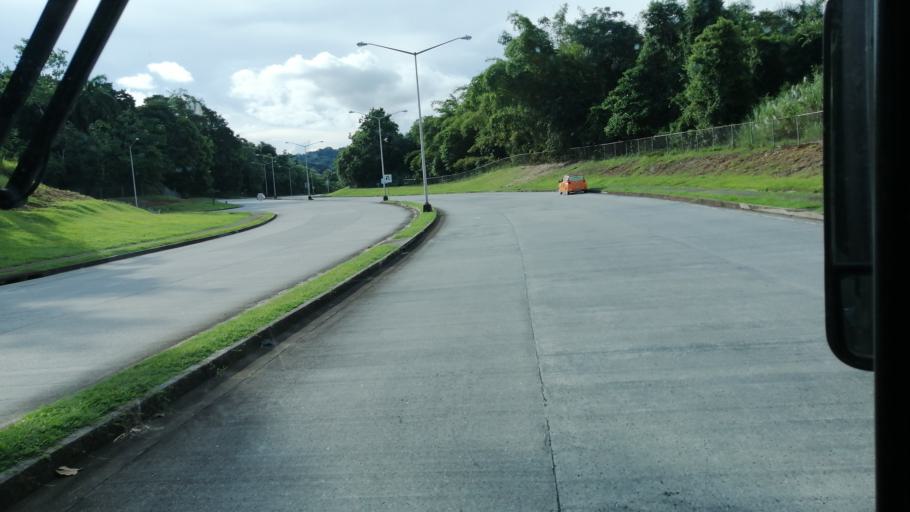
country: PA
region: Panama
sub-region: Distrito de Panama
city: Ancon
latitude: 8.9292
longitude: -79.5932
